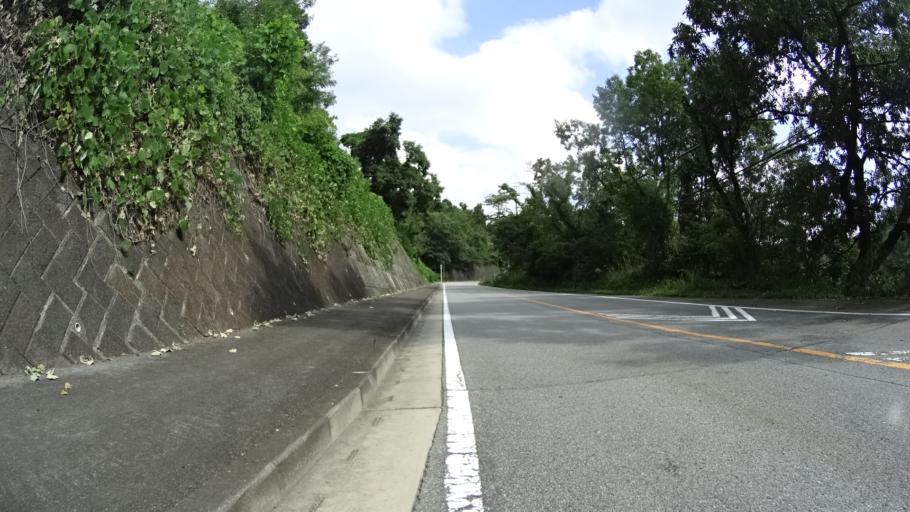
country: JP
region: Yamanashi
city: Kofu-shi
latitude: 35.7077
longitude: 138.5533
